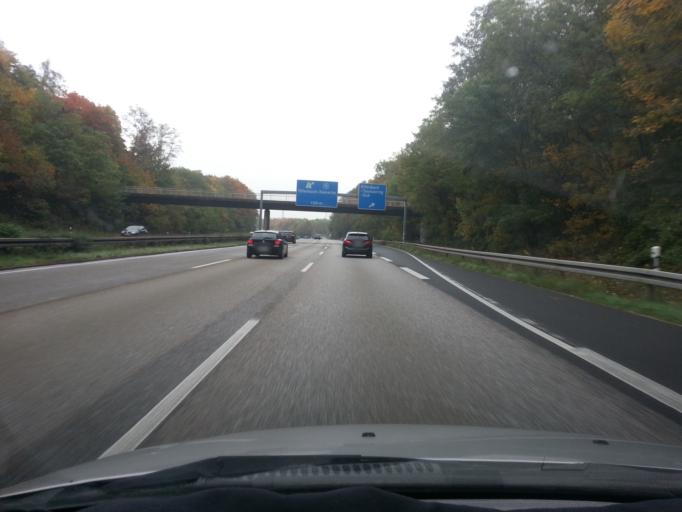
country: DE
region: Hesse
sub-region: Regierungsbezirk Darmstadt
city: Offenbach
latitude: 50.0915
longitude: 8.7396
